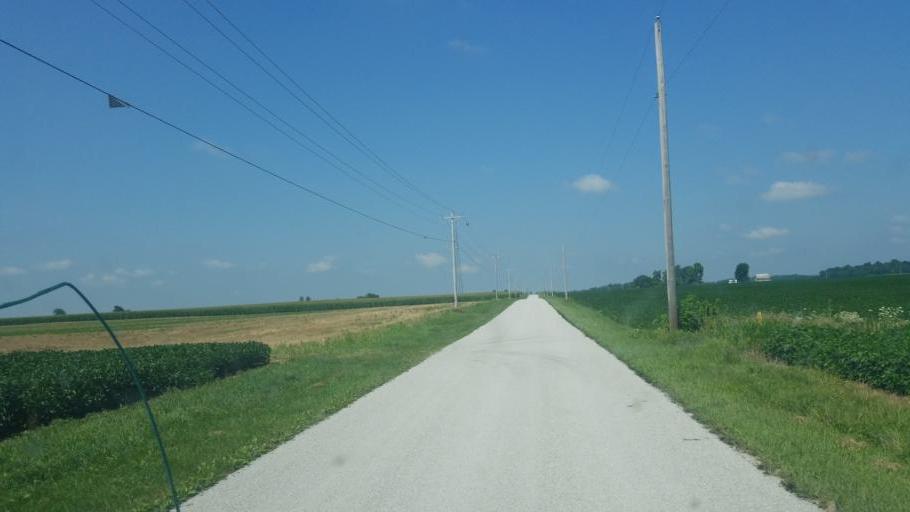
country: US
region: Ohio
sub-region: Hardin County
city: Kenton
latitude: 40.7036
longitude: -83.7013
